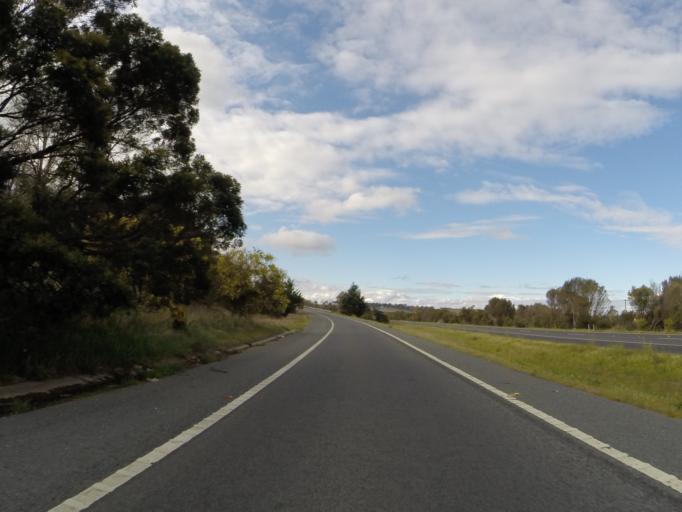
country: AU
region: New South Wales
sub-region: Wingecarribee
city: Bundanoon
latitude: -34.5896
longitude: 150.2474
